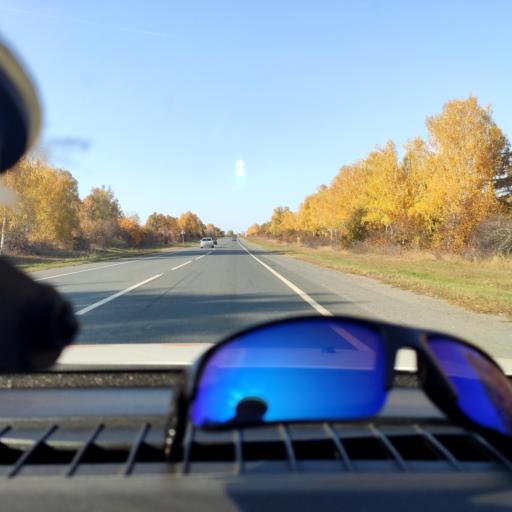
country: RU
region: Samara
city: Volzhskiy
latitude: 53.4690
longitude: 50.1248
